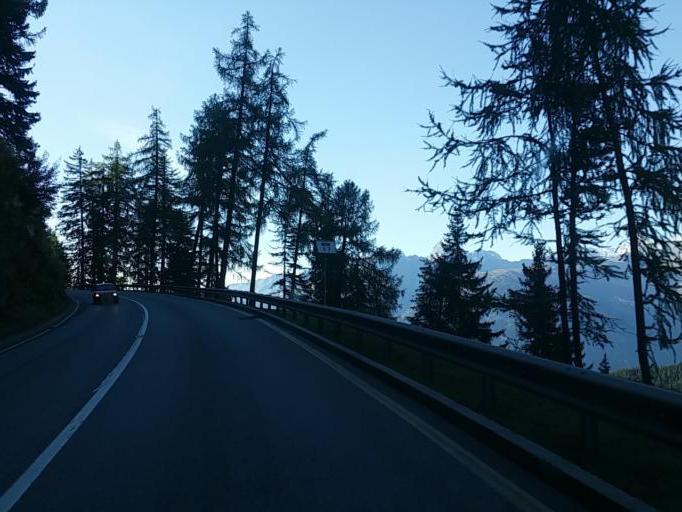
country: CH
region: Valais
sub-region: Brig District
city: Naters
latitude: 46.2848
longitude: 8.0432
